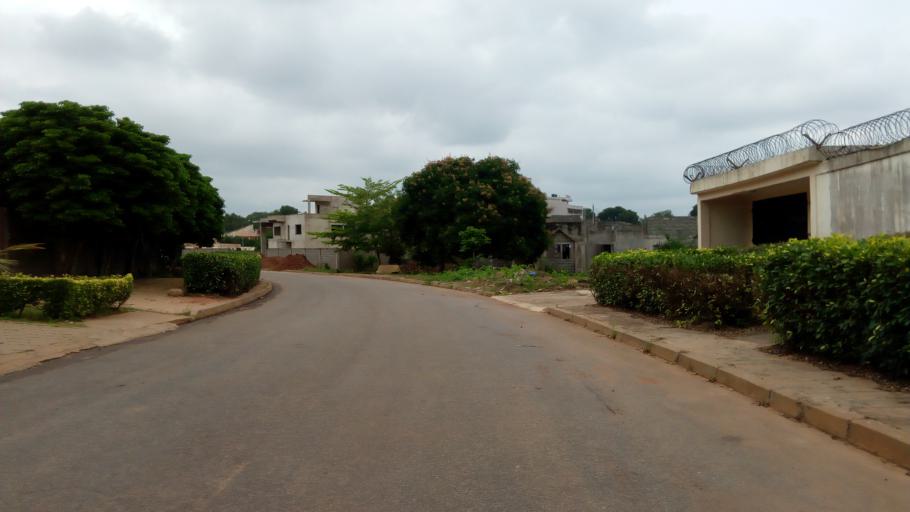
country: TG
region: Maritime
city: Lome
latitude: 6.1872
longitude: 1.2145
